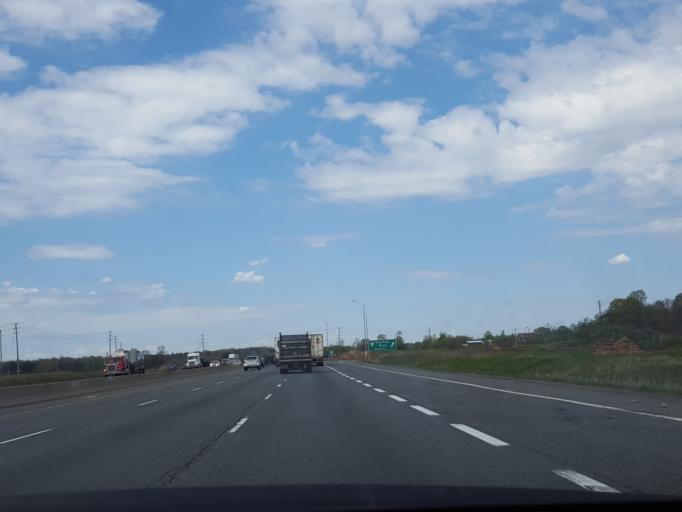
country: CA
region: Ontario
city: Oshawa
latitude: 43.8797
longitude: -78.7577
